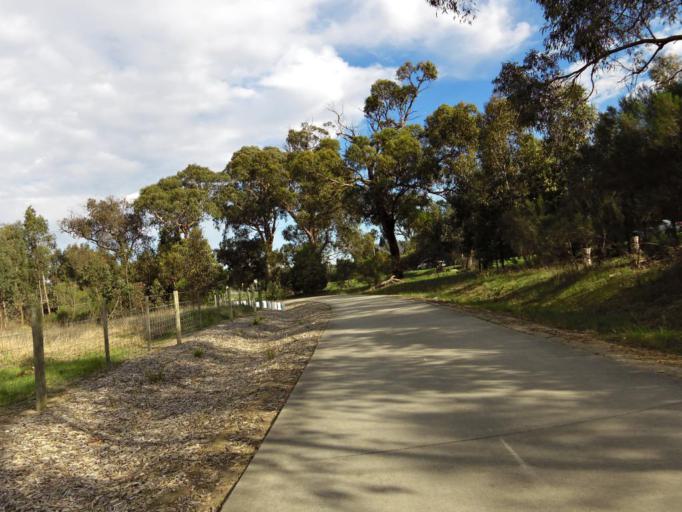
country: AU
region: Victoria
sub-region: Knox
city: Wantirna South
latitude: -37.8776
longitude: 145.2120
